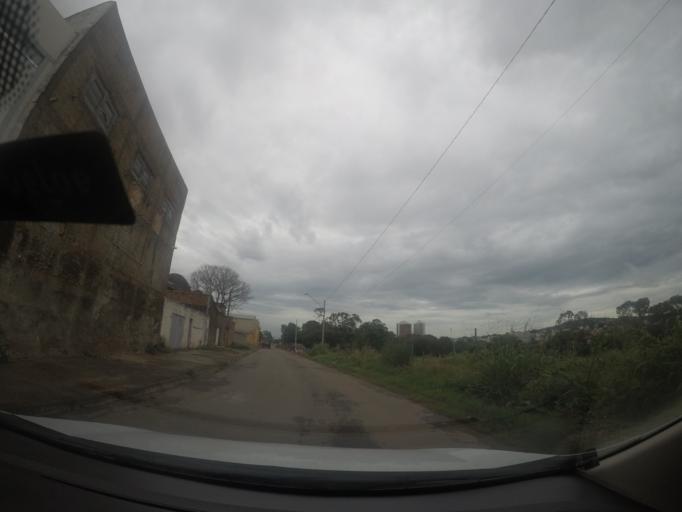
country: BR
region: Goias
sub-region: Goiania
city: Goiania
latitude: -16.6635
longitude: -49.3126
